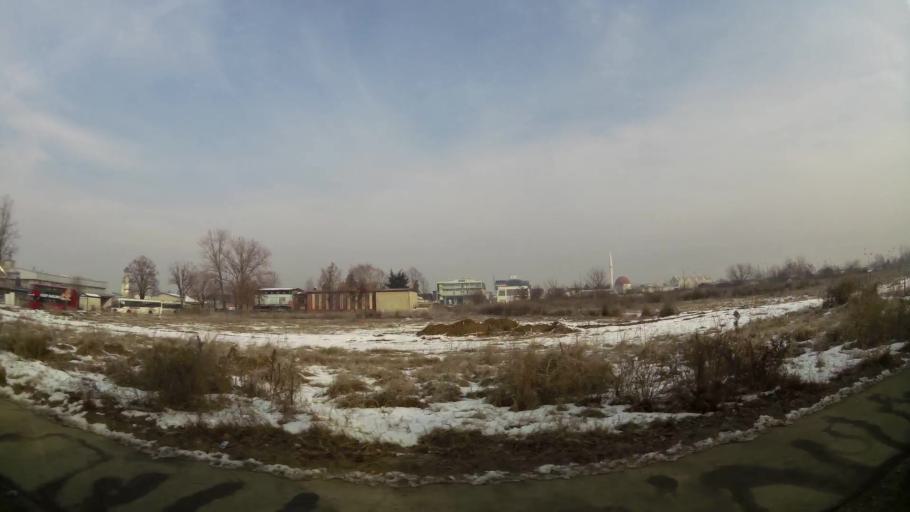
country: MK
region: Butel
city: Butel
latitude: 42.0250
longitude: 21.4403
